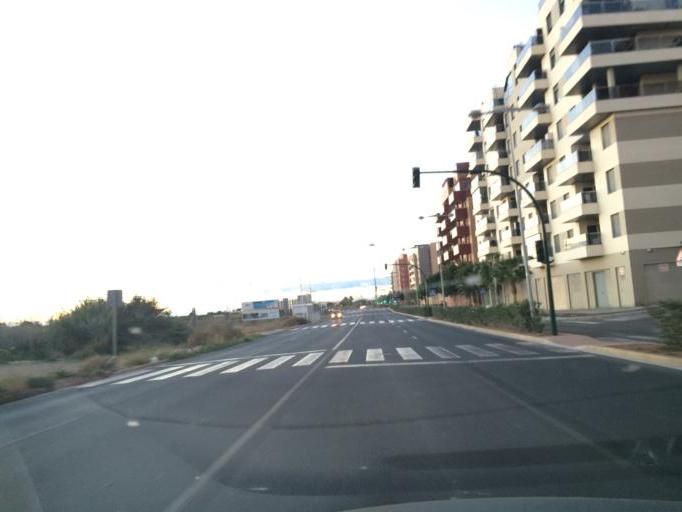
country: ES
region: Andalusia
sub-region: Provincia de Almeria
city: Almeria
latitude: 36.8347
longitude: -2.4383
